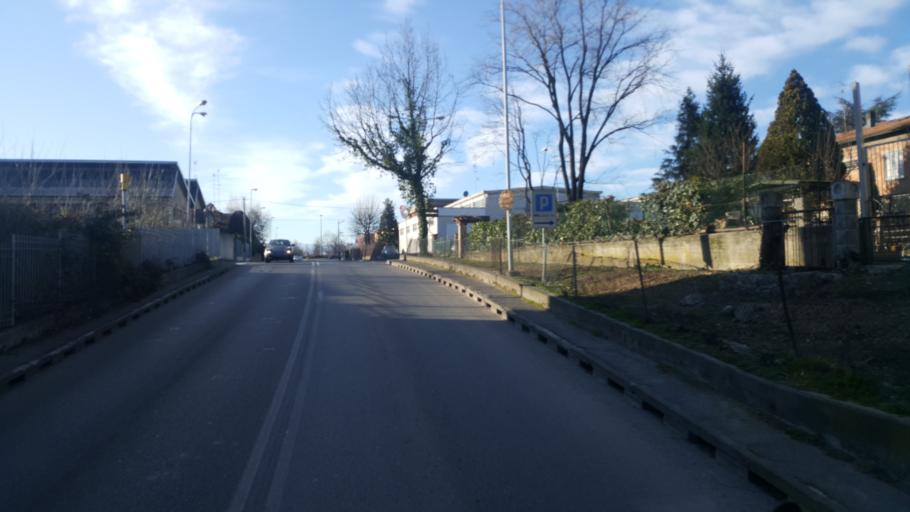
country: IT
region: Emilia-Romagna
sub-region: Provincia di Reggio Emilia
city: Rubiera
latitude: 44.6569
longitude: 10.7742
